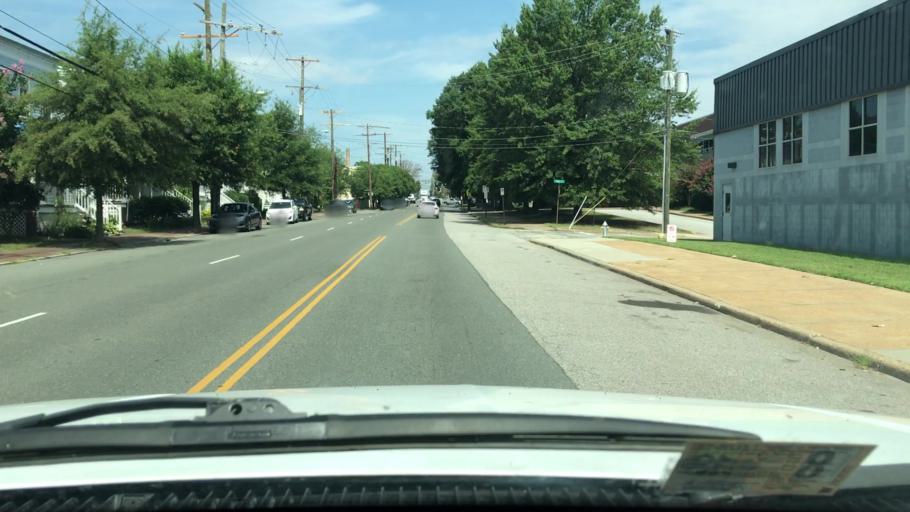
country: US
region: Virginia
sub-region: City of Richmond
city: Richmond
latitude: 37.5534
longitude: -77.4475
